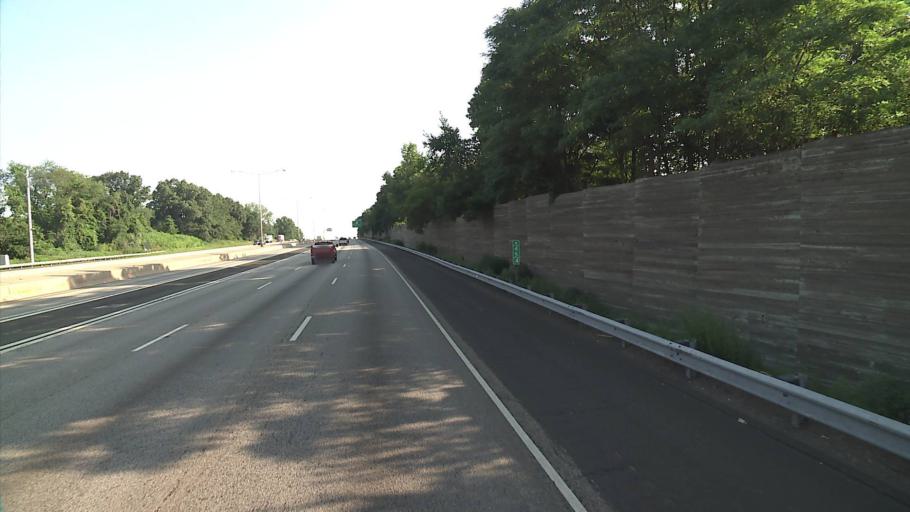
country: US
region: Connecticut
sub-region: Hartford County
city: Windsor
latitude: 41.8653
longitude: -72.6620
